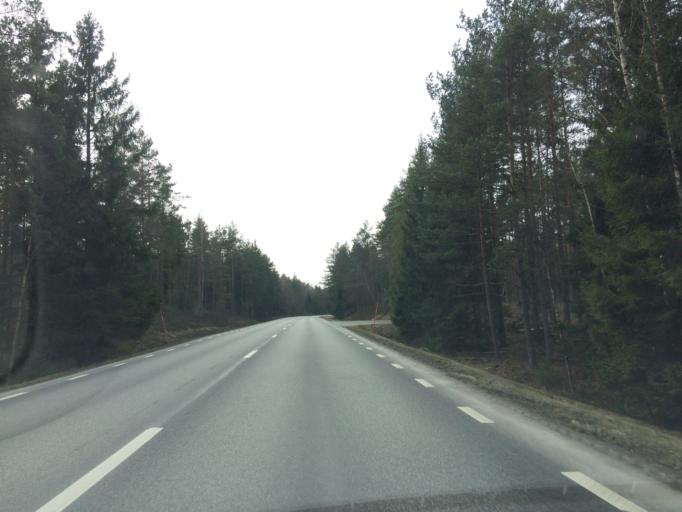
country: SE
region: Skane
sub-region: Osby Kommun
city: Lonsboda
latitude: 56.3864
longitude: 14.2750
